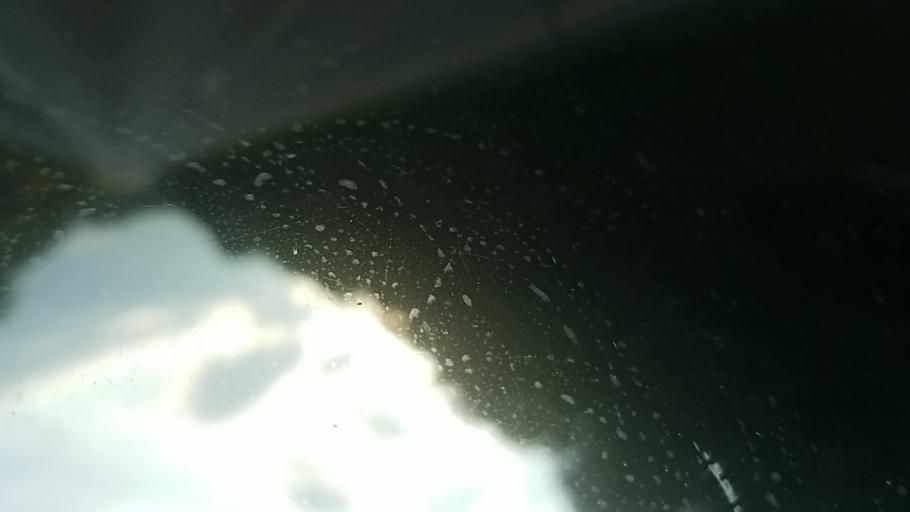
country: US
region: Pennsylvania
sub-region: Clearfield County
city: Troy
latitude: 40.9852
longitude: -78.1479
